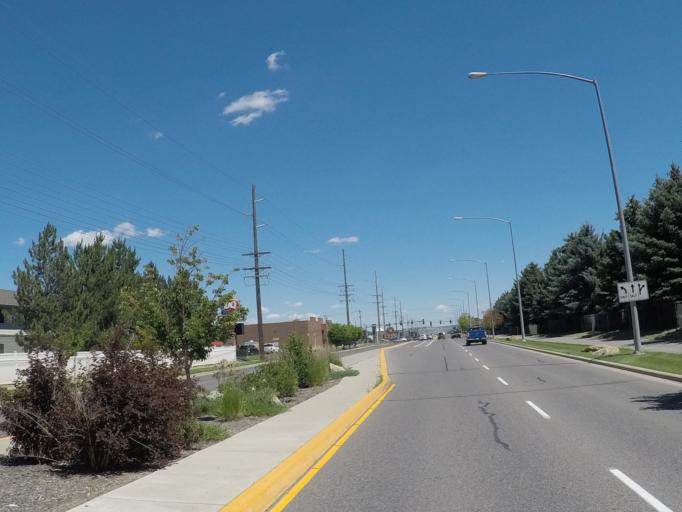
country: US
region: Montana
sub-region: Yellowstone County
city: Billings
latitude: 45.7551
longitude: -108.5995
